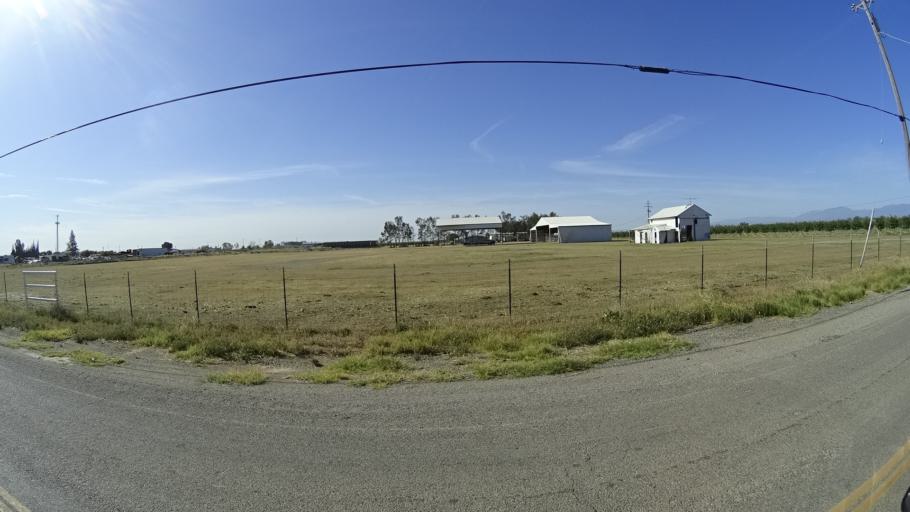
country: US
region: California
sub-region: Glenn County
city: Orland
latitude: 39.6970
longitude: -122.2005
